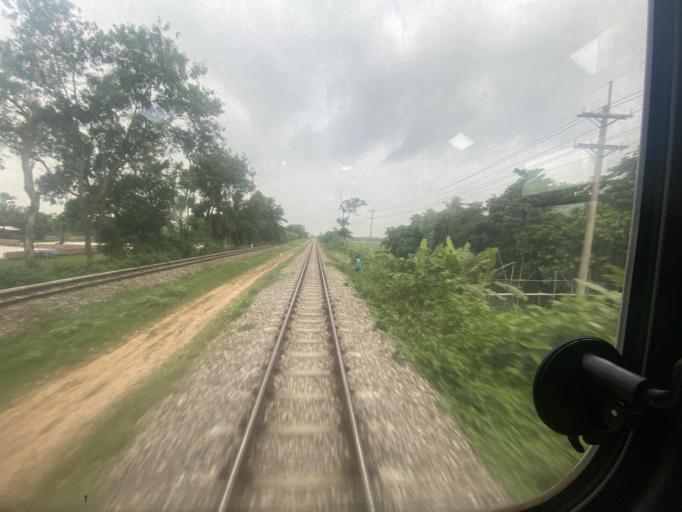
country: BD
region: Dhaka
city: Tungi
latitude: 23.9329
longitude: 90.5104
